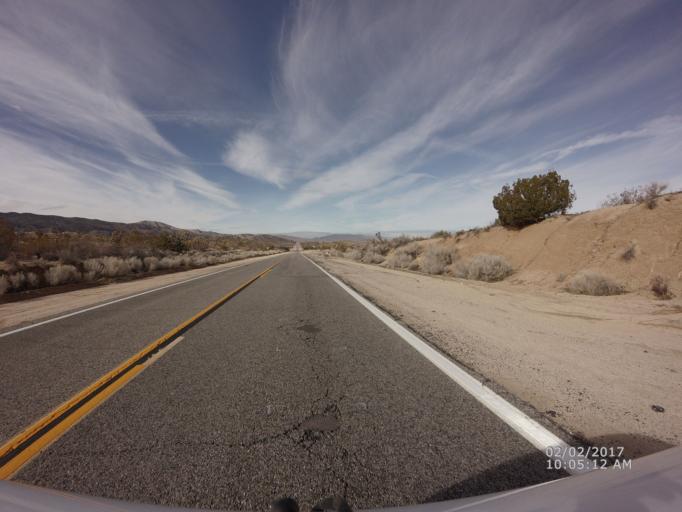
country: US
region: California
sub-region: Los Angeles County
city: Littlerock
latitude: 34.5066
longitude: -117.9851
